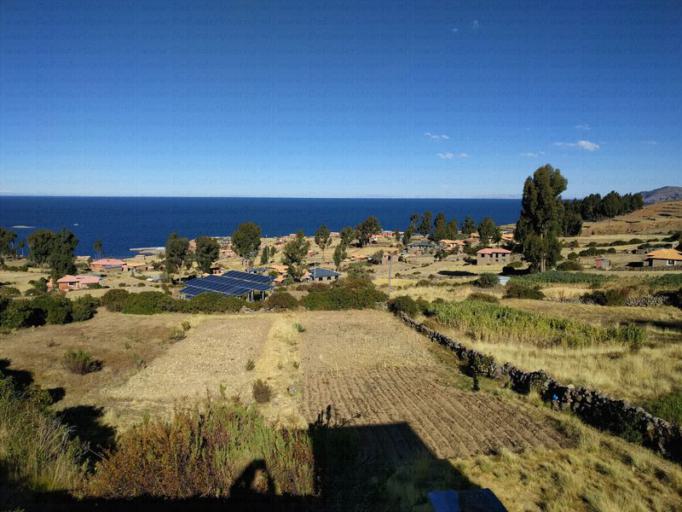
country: PE
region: Puno
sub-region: Provincia de Puno
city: Taquile
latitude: -15.6684
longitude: -69.7067
